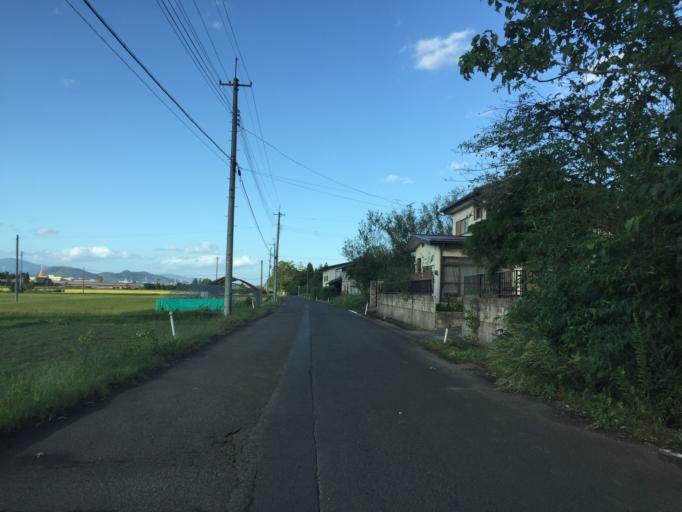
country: JP
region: Fukushima
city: Fukushima-shi
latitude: 37.7079
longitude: 140.4395
